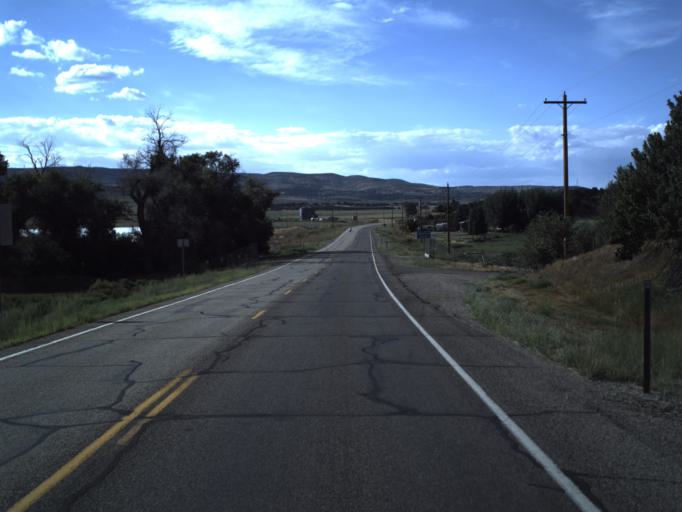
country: US
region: Utah
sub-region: Sanpete County
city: Fairview
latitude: 39.6378
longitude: -111.4457
